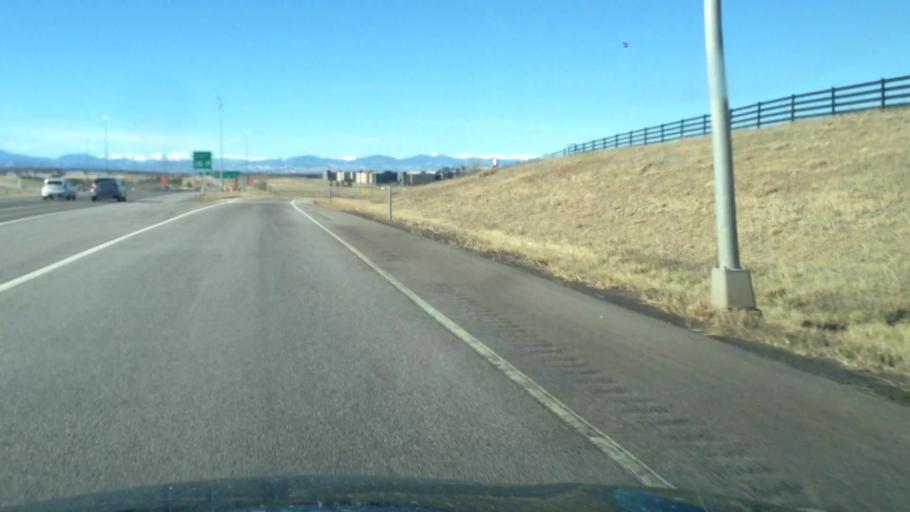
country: US
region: Colorado
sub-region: Douglas County
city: Meridian
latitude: 39.5523
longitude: -104.8569
